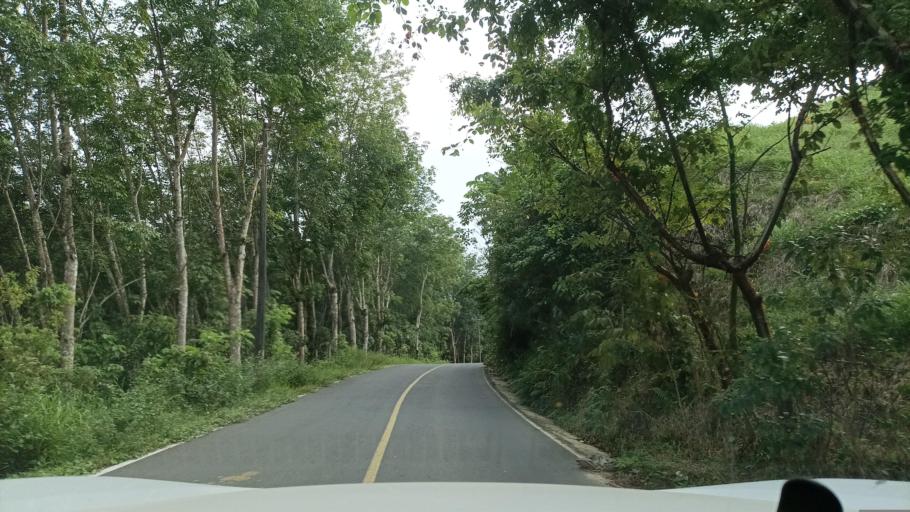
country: MX
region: Veracruz
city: Hidalgotitlan
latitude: 17.6904
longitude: -94.4567
